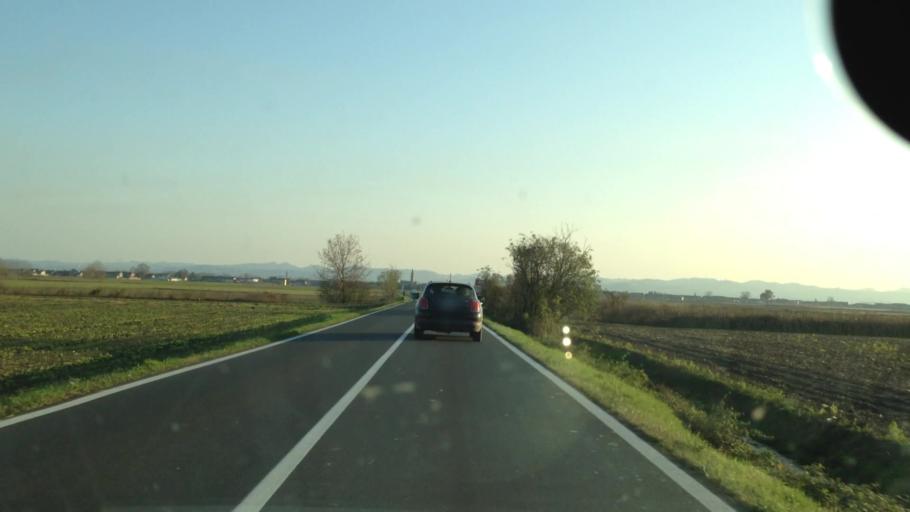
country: IT
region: Piedmont
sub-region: Provincia di Vercelli
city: Lamporo
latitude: 45.2438
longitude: 8.0910
